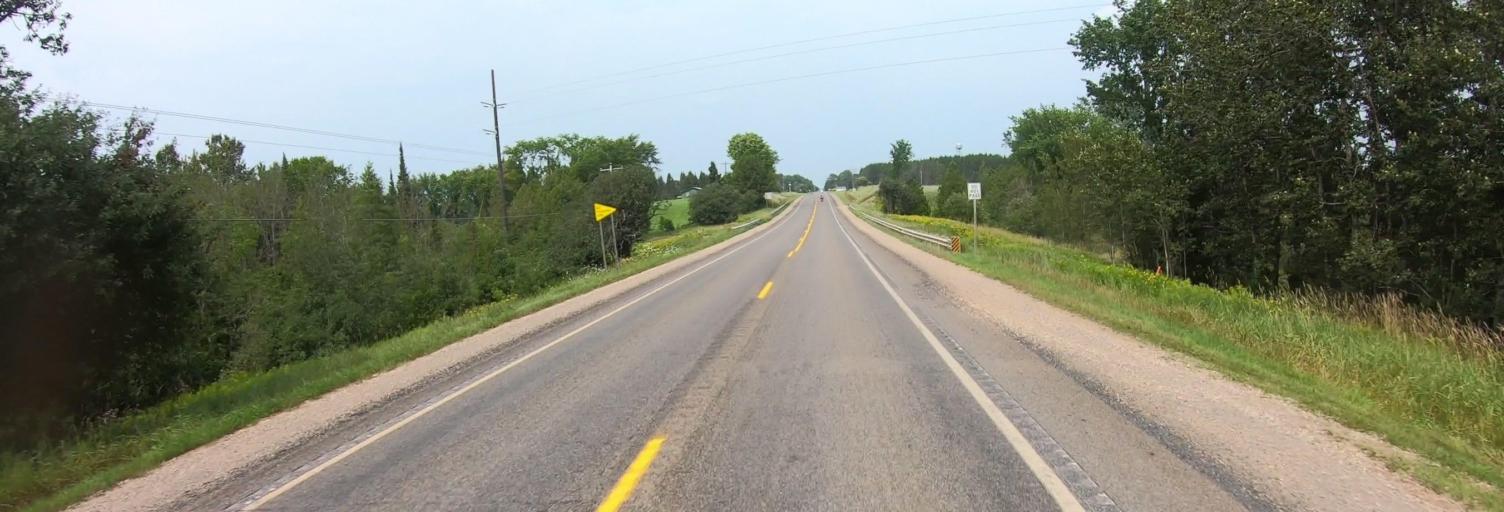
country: US
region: Michigan
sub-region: Alger County
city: Munising
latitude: 46.3365
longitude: -86.9289
